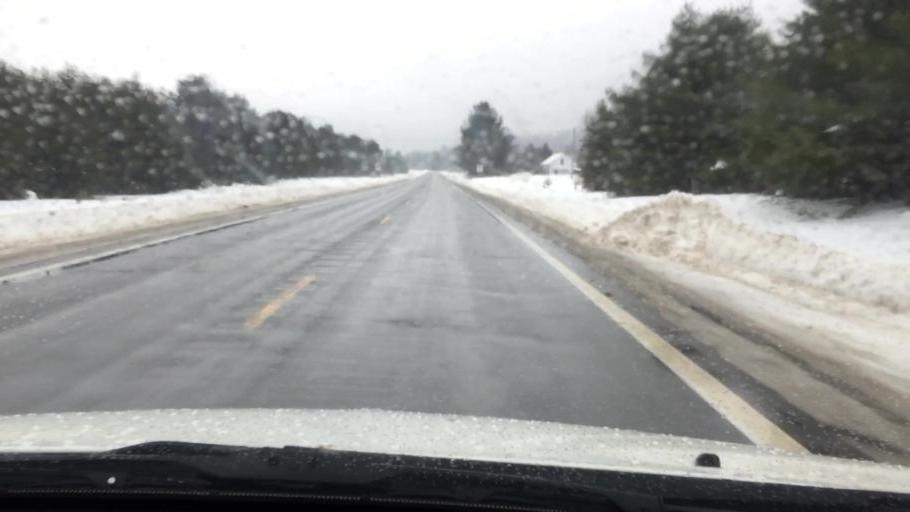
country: US
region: Michigan
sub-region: Charlevoix County
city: East Jordan
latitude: 45.0743
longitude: -85.0870
